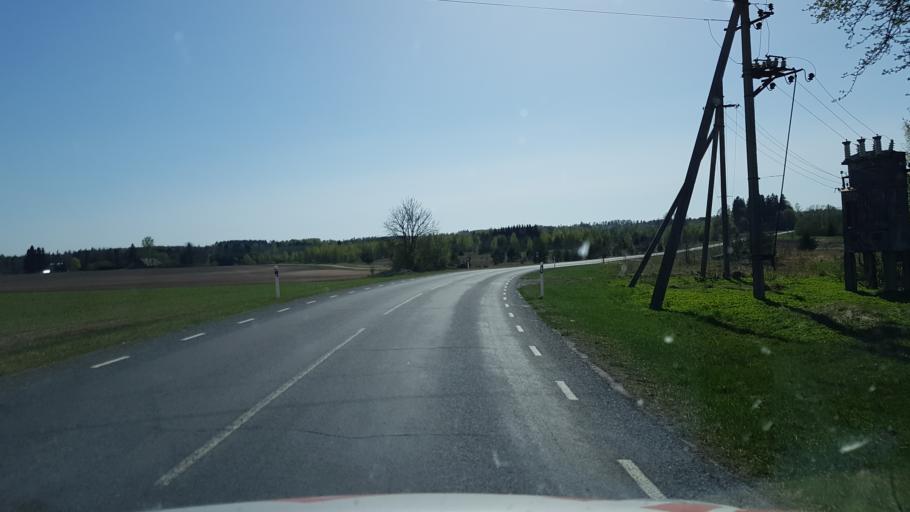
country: EE
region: Viljandimaa
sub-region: Viljandi linn
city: Viljandi
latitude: 58.3138
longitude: 25.5627
